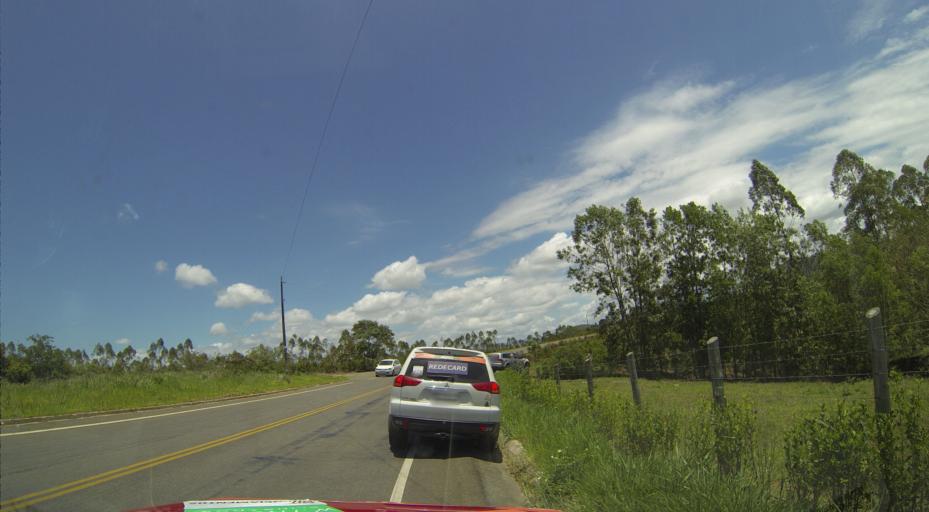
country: BR
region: Espirito Santo
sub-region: Serra
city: Serra
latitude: -20.0109
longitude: -40.2293
